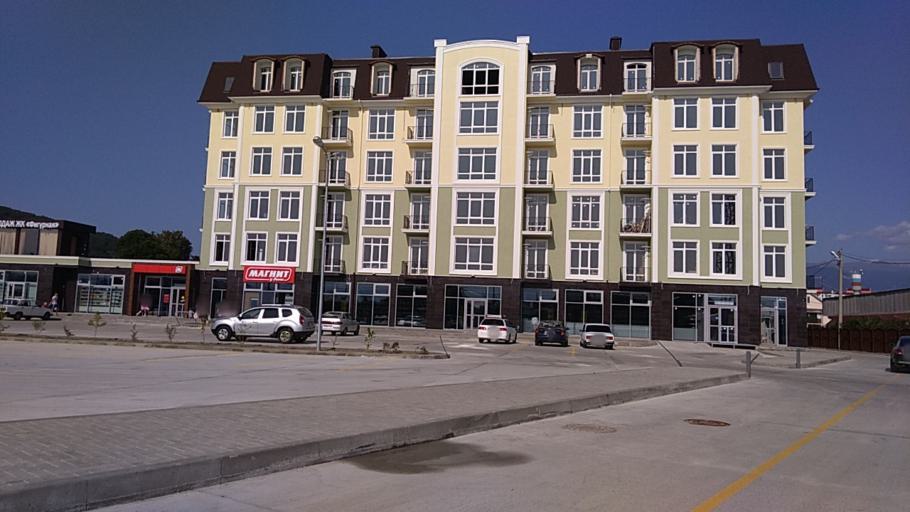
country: RU
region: Krasnodarskiy
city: Vysokoye
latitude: 43.3975
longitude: 39.9956
